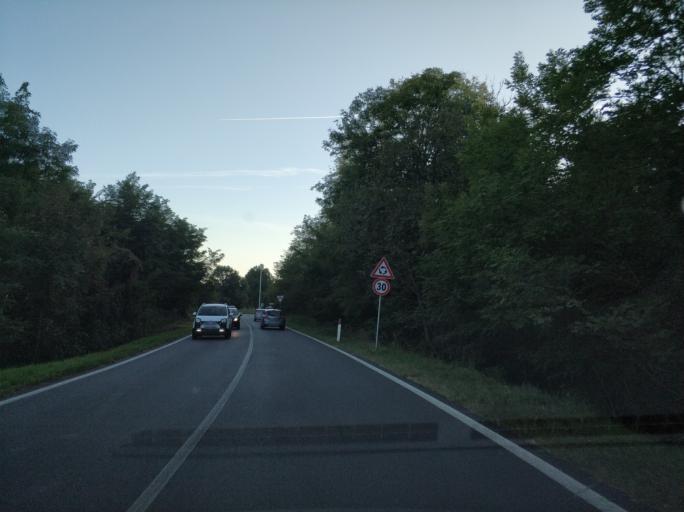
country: IT
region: Piedmont
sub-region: Provincia di Torino
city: Villanova Canavese
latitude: 45.2374
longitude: 7.5457
